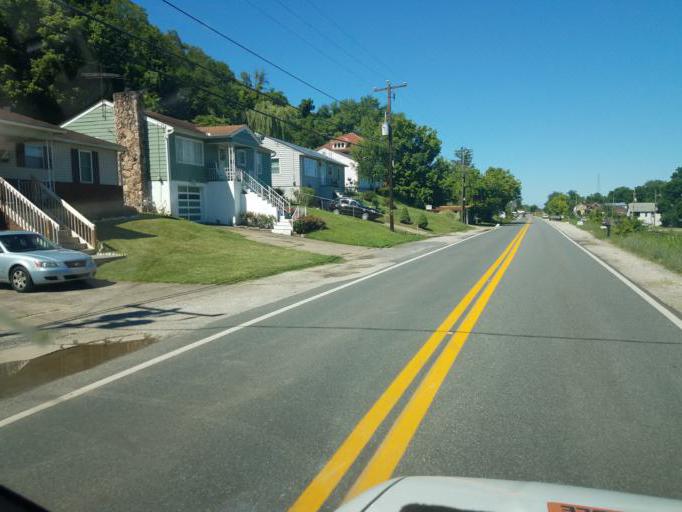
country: US
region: West Virginia
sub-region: Cabell County
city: Pea Ridge
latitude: 38.4348
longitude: -82.3541
